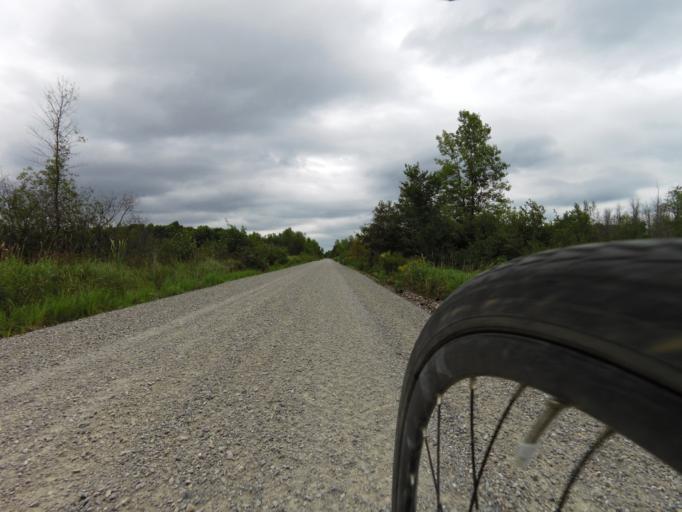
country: CA
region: Ontario
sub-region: Lanark County
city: Smiths Falls
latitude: 44.9450
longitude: -76.0414
